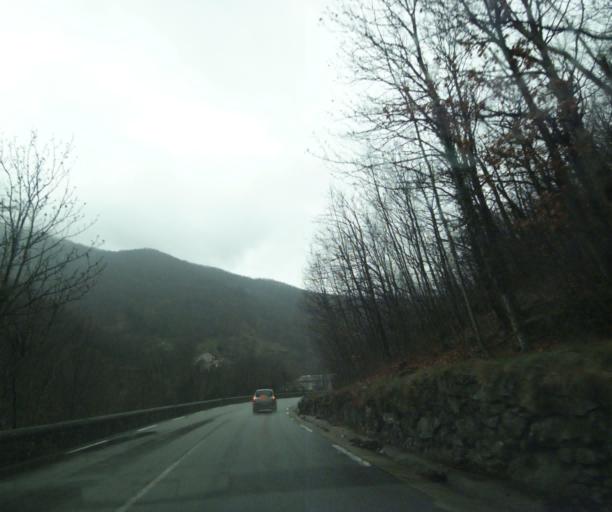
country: FR
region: Rhone-Alpes
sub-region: Departement de l'Ardeche
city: Thueyts
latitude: 44.6652
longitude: 4.1498
